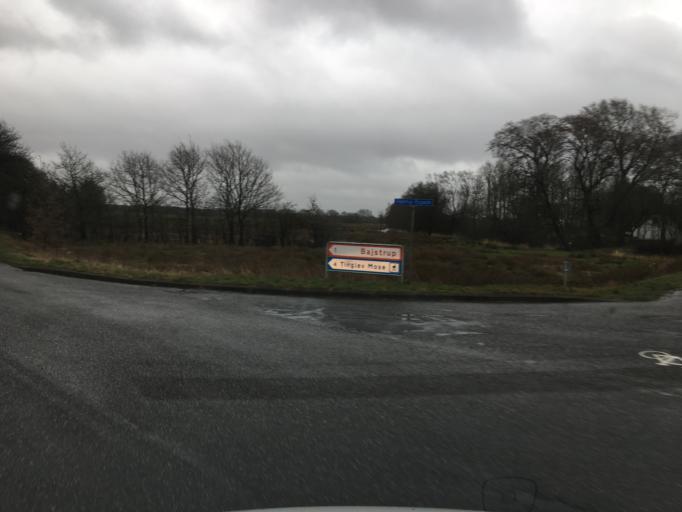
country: DK
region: South Denmark
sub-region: Aabenraa Kommune
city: Tinglev
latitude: 54.9036
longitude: 9.2563
